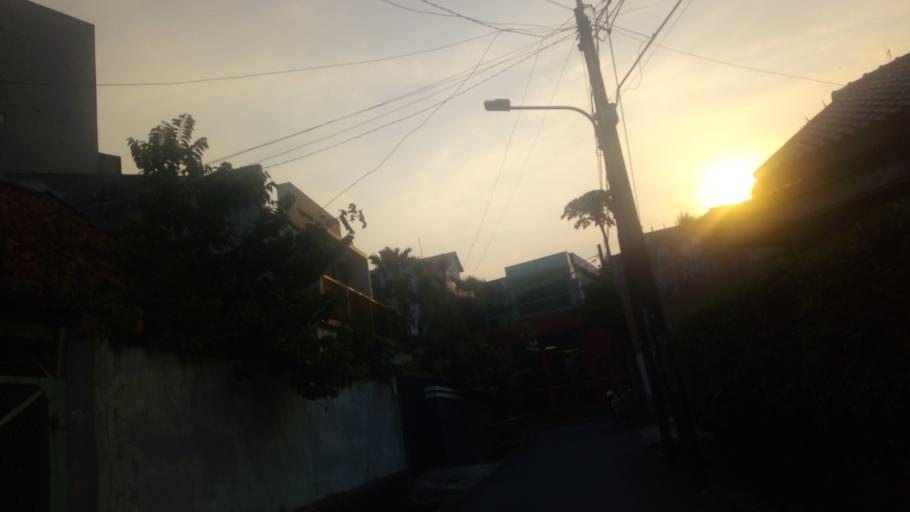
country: ID
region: Jakarta Raya
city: Jakarta
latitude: -6.2020
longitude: 106.8493
